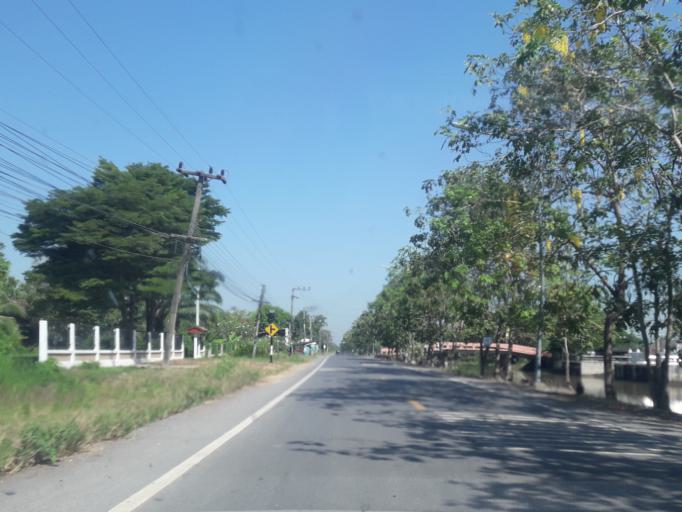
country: TH
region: Pathum Thani
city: Nong Suea
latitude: 14.1660
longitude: 100.8459
